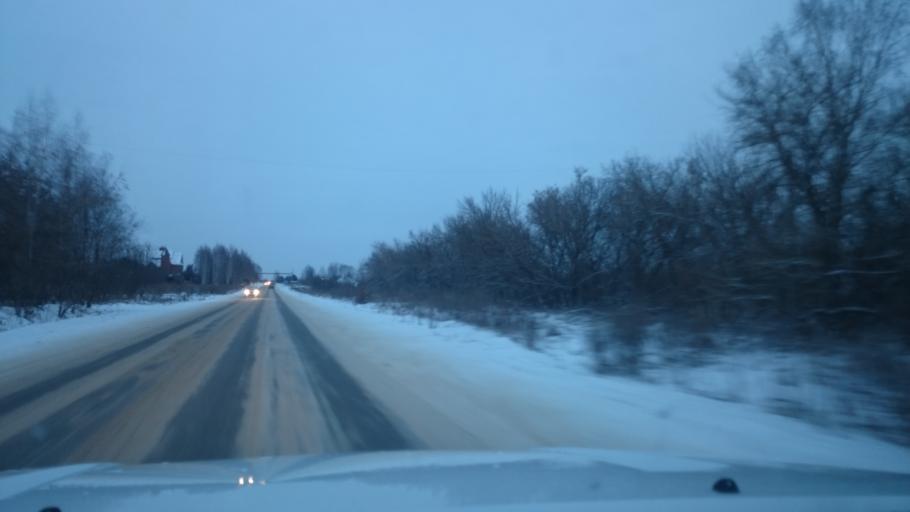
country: RU
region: Tula
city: Leninskiy
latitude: 54.2499
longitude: 37.3818
